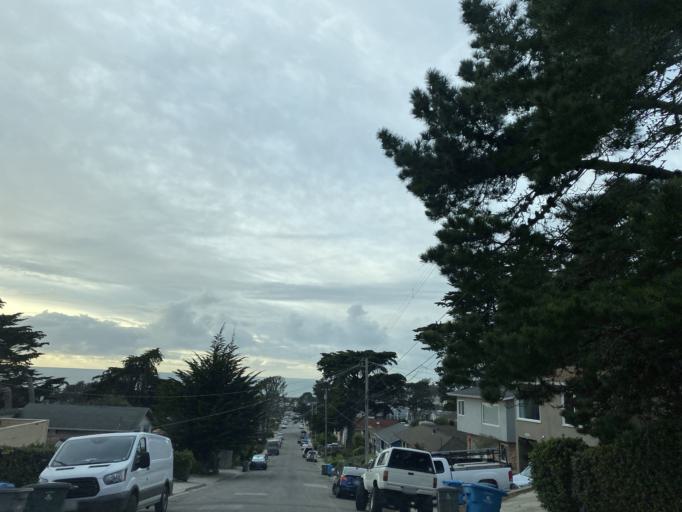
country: US
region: California
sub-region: San Mateo County
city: Broadmoor
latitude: 37.6520
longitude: -122.4844
